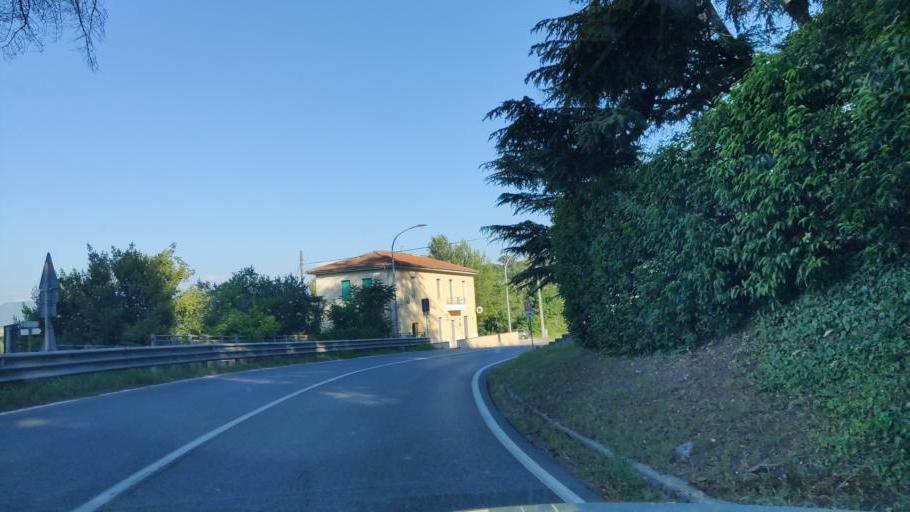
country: IT
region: Umbria
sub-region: Provincia di Terni
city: Narni Scalo
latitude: 42.5243
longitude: 12.5161
